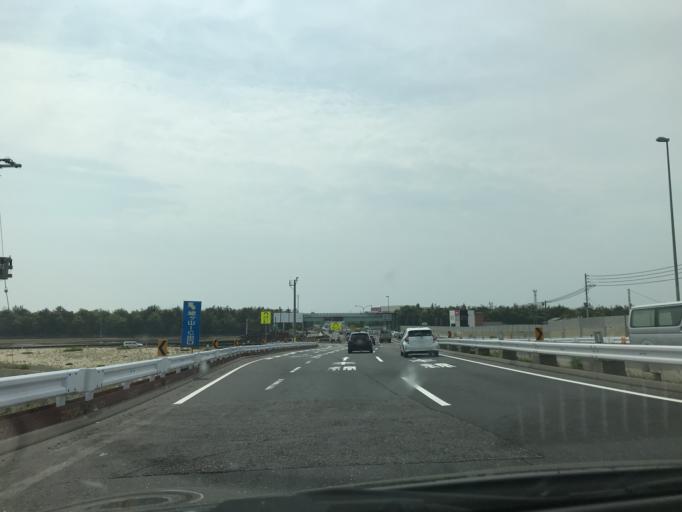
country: JP
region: Niigata
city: Kameda-honcho
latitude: 37.8836
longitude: 139.0799
